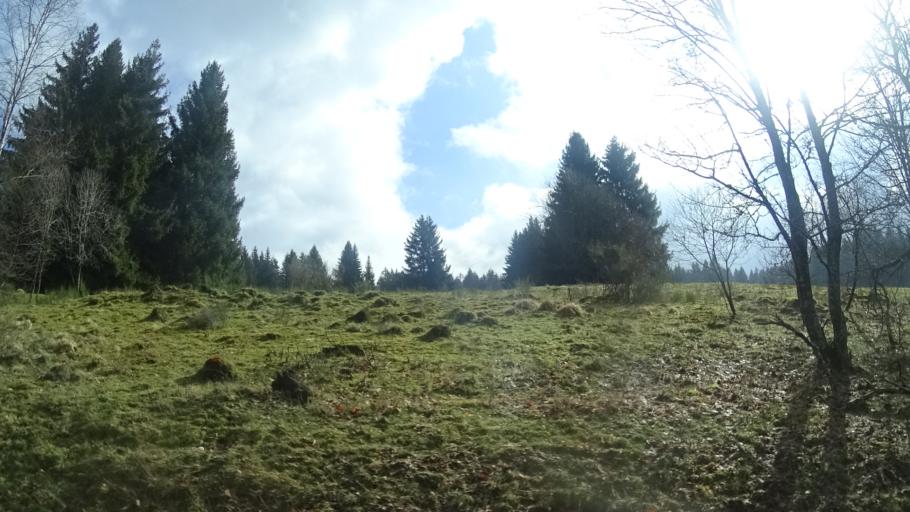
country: DE
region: Rheinland-Pfalz
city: Borfink
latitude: 49.7084
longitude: 7.1021
